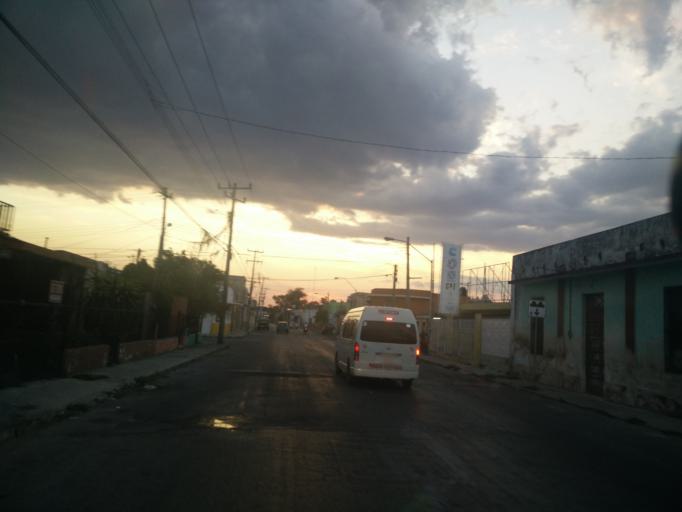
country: MX
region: Yucatan
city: Merida
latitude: 20.9636
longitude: -89.6358
